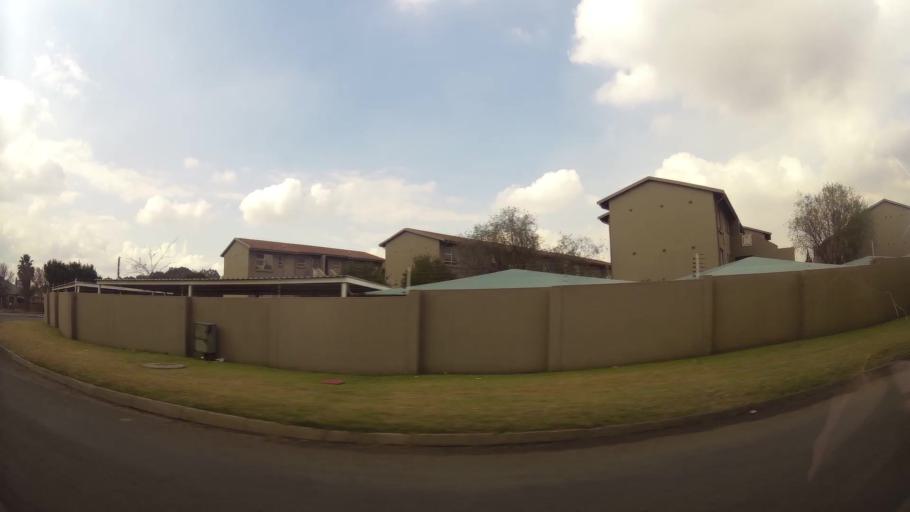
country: ZA
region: Gauteng
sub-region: Sedibeng District Municipality
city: Vereeniging
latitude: -26.6714
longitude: 27.9391
